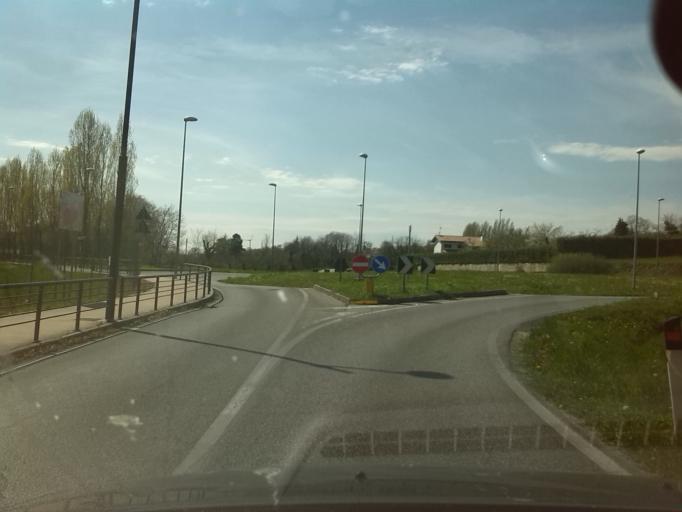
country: IT
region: Friuli Venezia Giulia
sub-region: Provincia di Udine
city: Pagnacco
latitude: 46.1237
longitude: 13.1809
